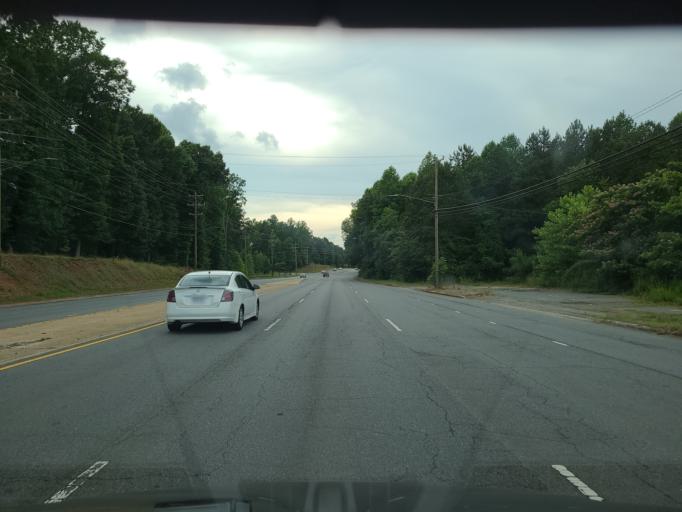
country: US
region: North Carolina
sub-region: Gaston County
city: Belmont
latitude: 35.2355
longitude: -80.9490
